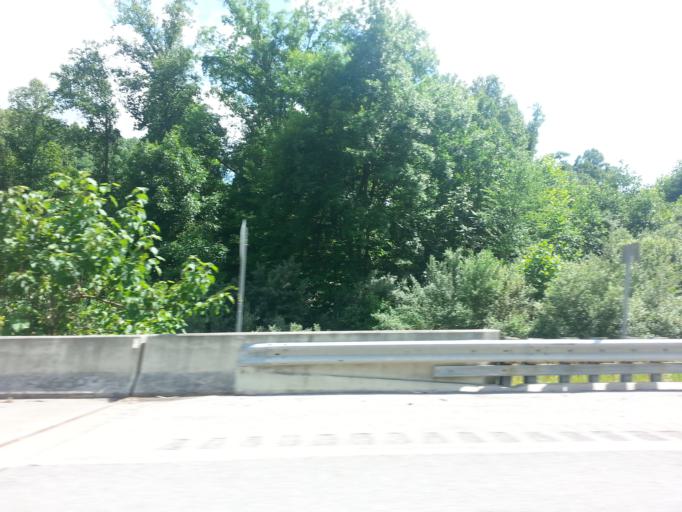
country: US
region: Kentucky
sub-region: Harlan County
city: Harlan
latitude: 36.7820
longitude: -83.2359
